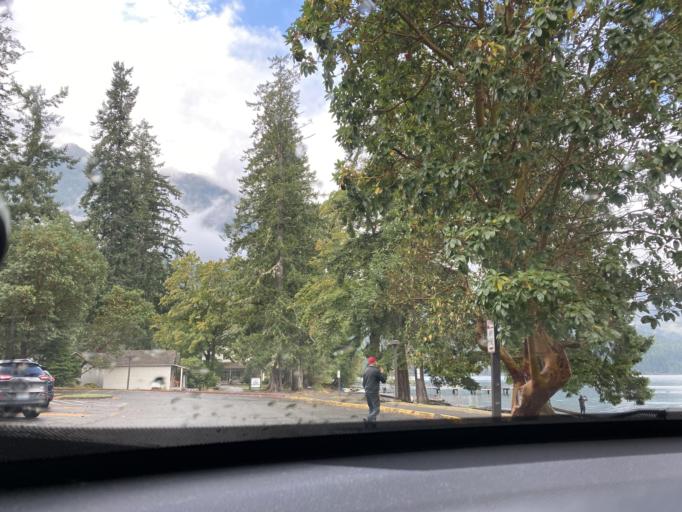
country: CA
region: British Columbia
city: Sooke
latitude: 48.0583
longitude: -123.7991
